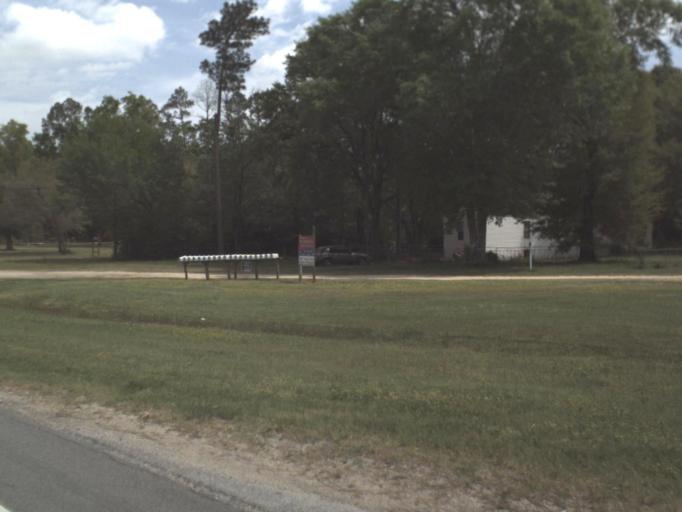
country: US
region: Florida
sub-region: Escambia County
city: Cantonment
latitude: 30.5344
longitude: -87.4168
